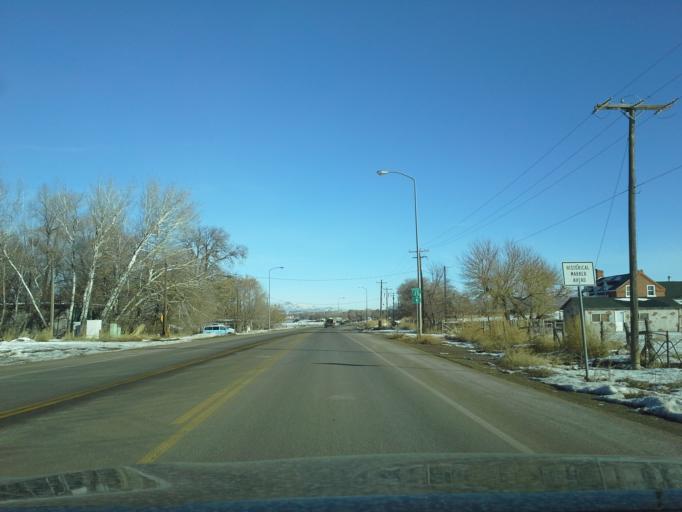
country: US
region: Utah
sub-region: Beaver County
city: Beaver
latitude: 38.2526
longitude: -112.6463
